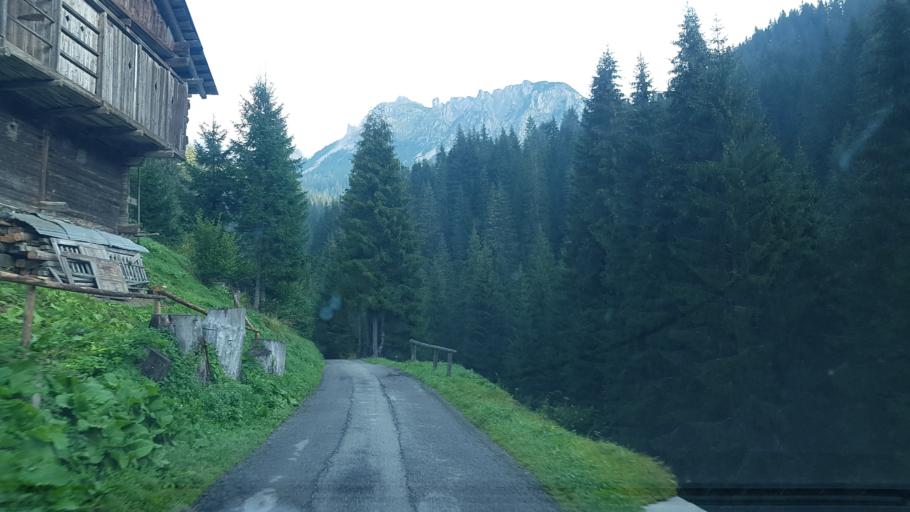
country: IT
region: Veneto
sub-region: Provincia di Belluno
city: San Pietro di Cadore
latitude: 46.5909
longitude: 12.5809
